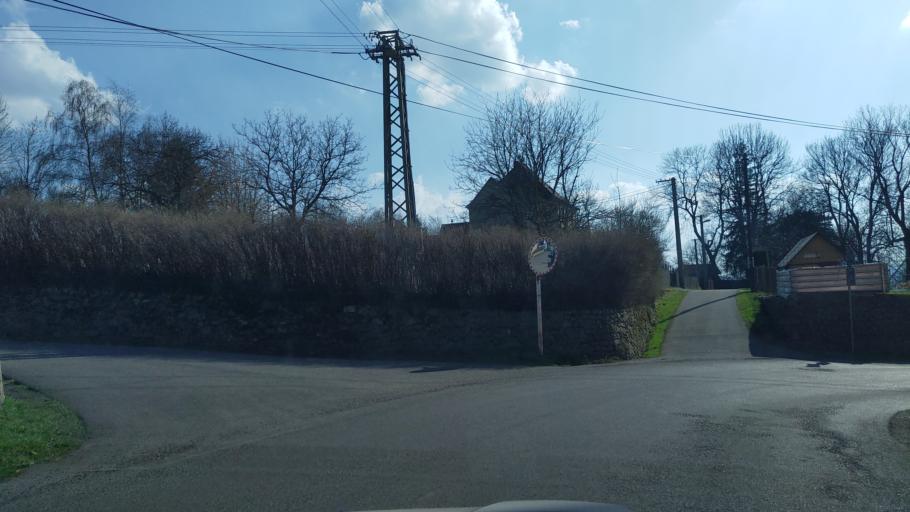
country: CZ
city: Kamenicky Senov
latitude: 50.7637
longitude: 14.4374
